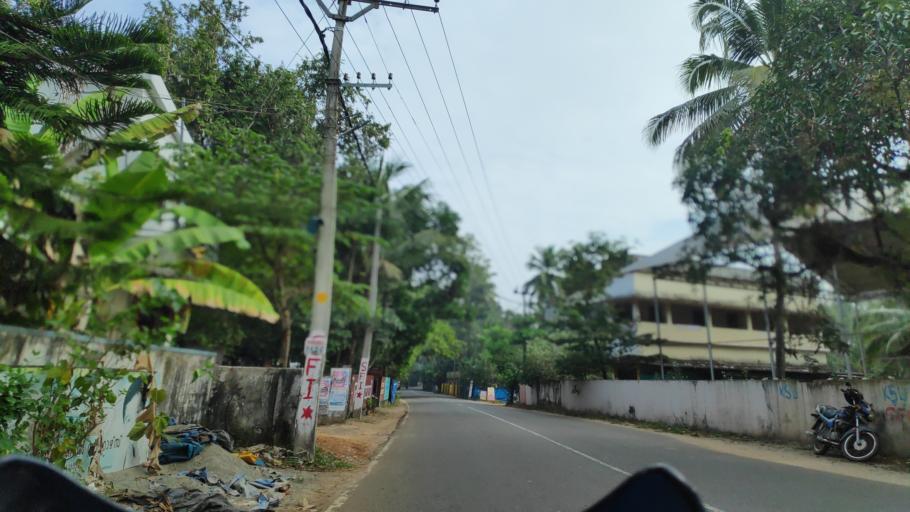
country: IN
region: Kerala
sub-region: Alappuzha
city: Shertallai
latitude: 9.7032
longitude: 76.3558
